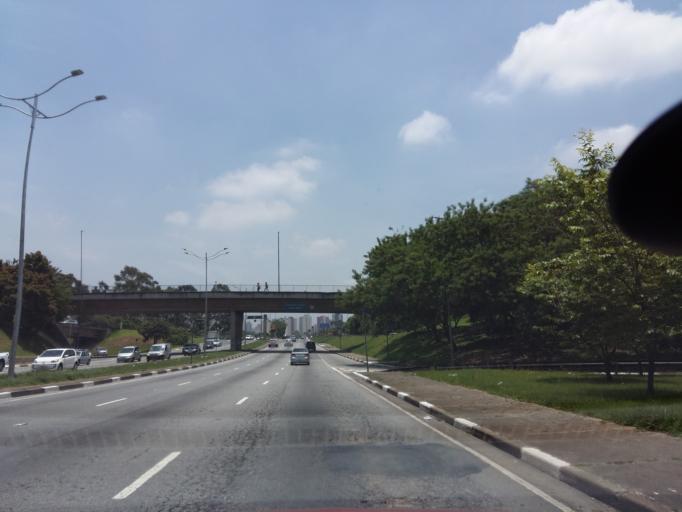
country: BR
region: Sao Paulo
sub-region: Diadema
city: Diadema
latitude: -23.6287
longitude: -46.6272
